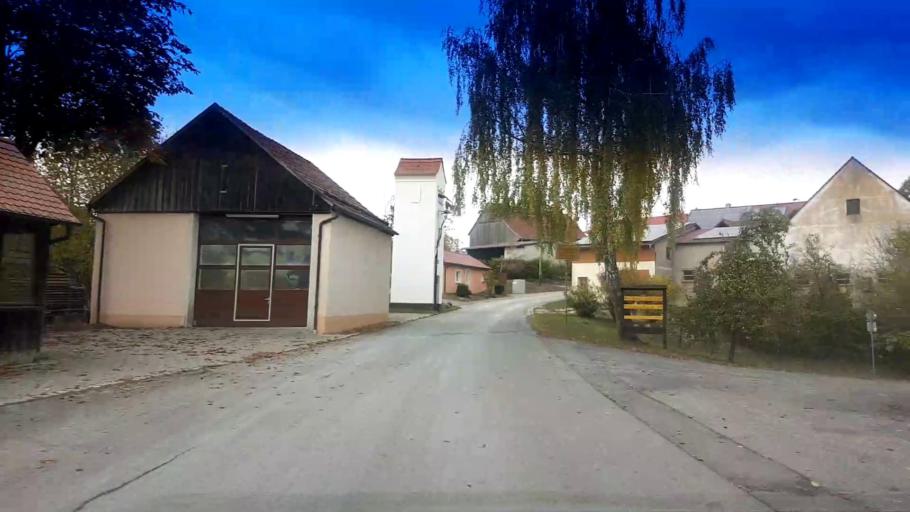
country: DE
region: Bavaria
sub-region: Upper Franconia
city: Wattendorf
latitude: 50.0209
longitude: 11.1030
